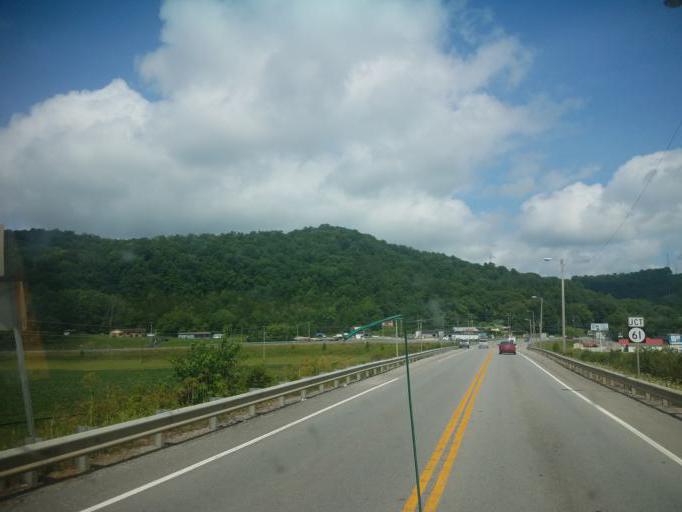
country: US
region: Kentucky
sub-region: Cumberland County
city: Burkesville
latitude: 36.7812
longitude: -85.3714
